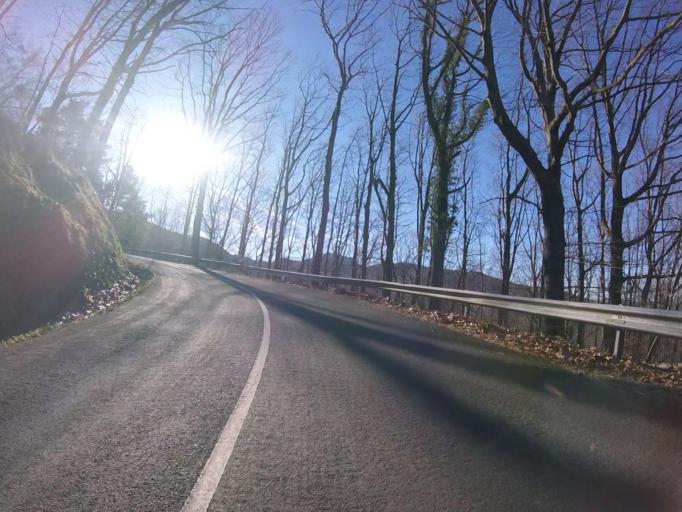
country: ES
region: Basque Country
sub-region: Provincia de Guipuzcoa
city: Irun
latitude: 43.3161
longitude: -1.7624
